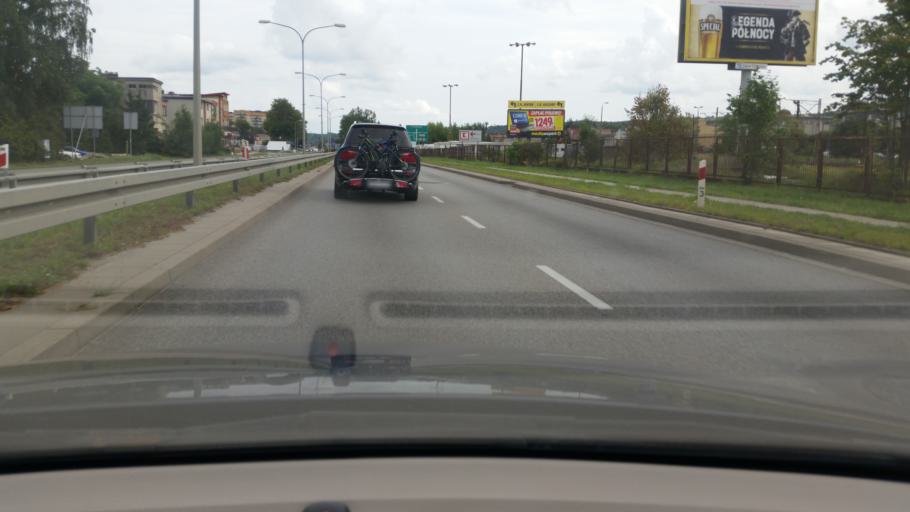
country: PL
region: Pomeranian Voivodeship
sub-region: Powiat wejherowski
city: Wejherowo
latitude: 54.6058
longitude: 18.2371
